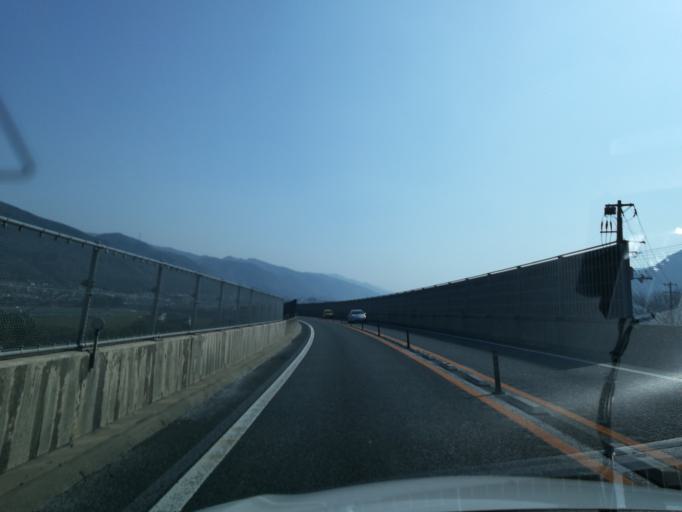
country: JP
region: Tokushima
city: Ikedacho
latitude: 34.0319
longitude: 133.8605
